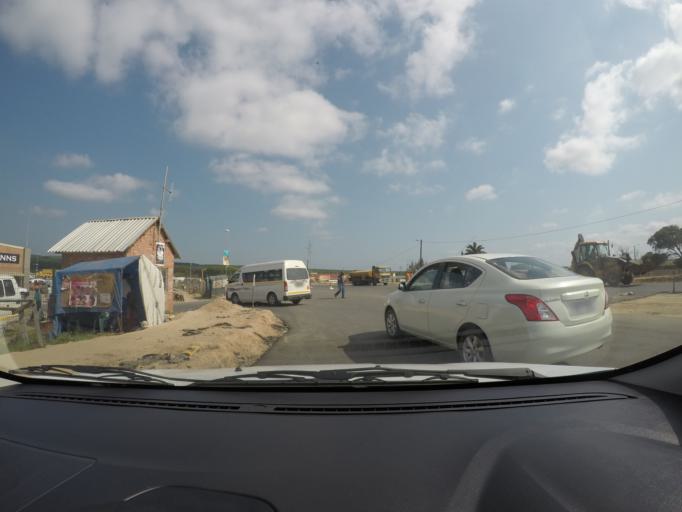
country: ZA
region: KwaZulu-Natal
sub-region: uThungulu District Municipality
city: eSikhawini
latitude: -28.8720
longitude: 31.9010
